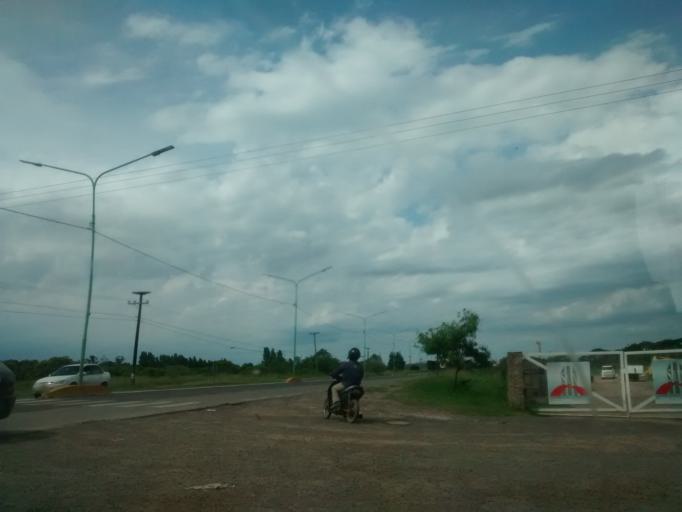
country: AR
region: Chaco
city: Resistencia
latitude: -27.4226
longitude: -58.9757
